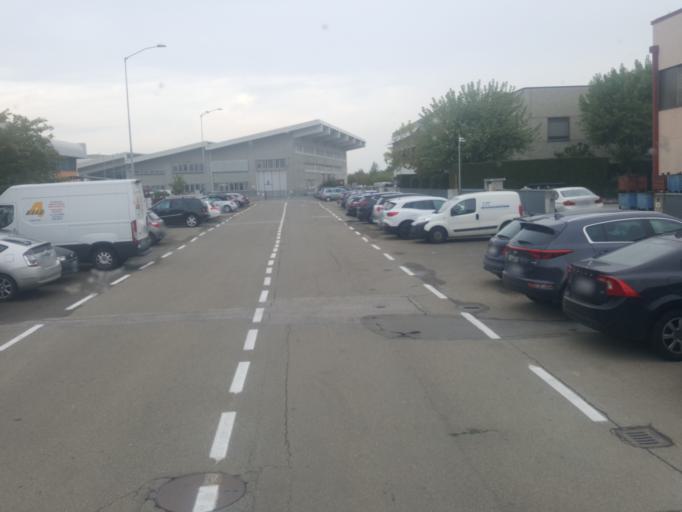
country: IT
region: Emilia-Romagna
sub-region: Provincia di Modena
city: Nonantola
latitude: 44.6787
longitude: 11.0254
